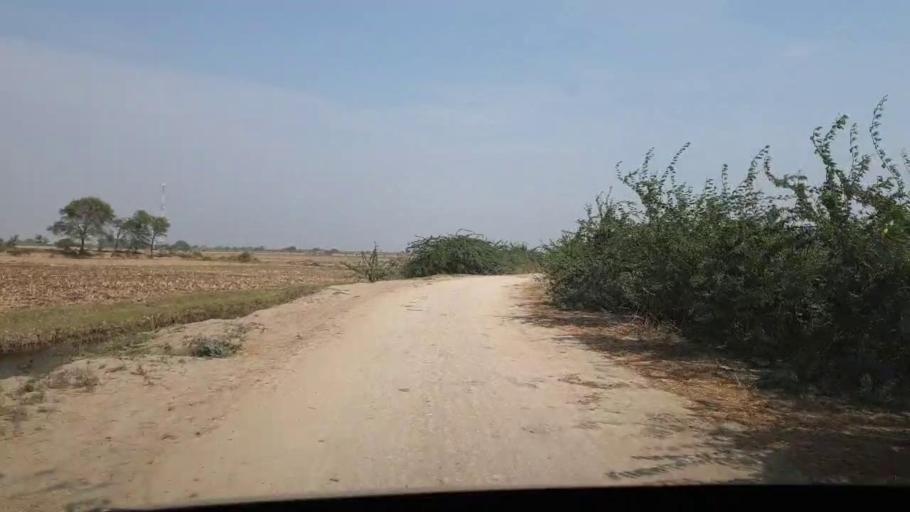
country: PK
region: Sindh
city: Chuhar Jamali
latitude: 24.2656
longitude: 67.9457
